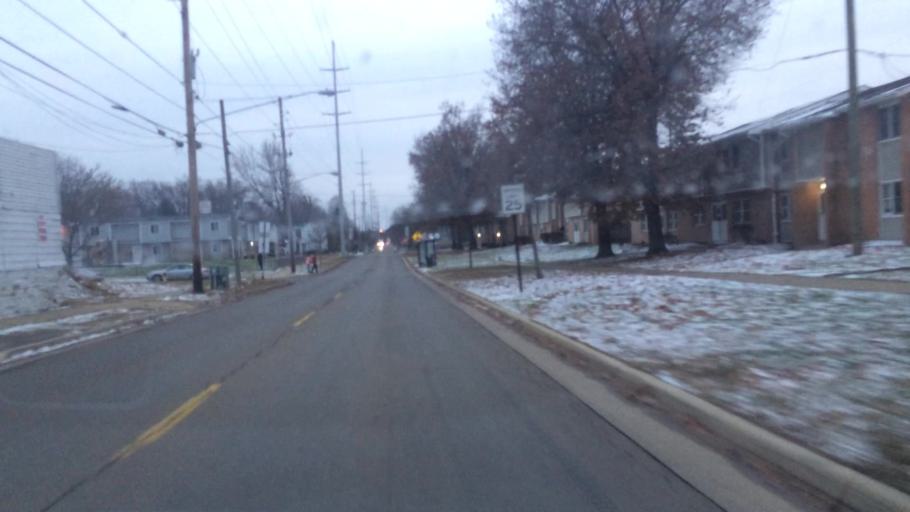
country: US
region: Ohio
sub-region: Summit County
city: Akron
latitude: 41.0558
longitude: -81.5413
